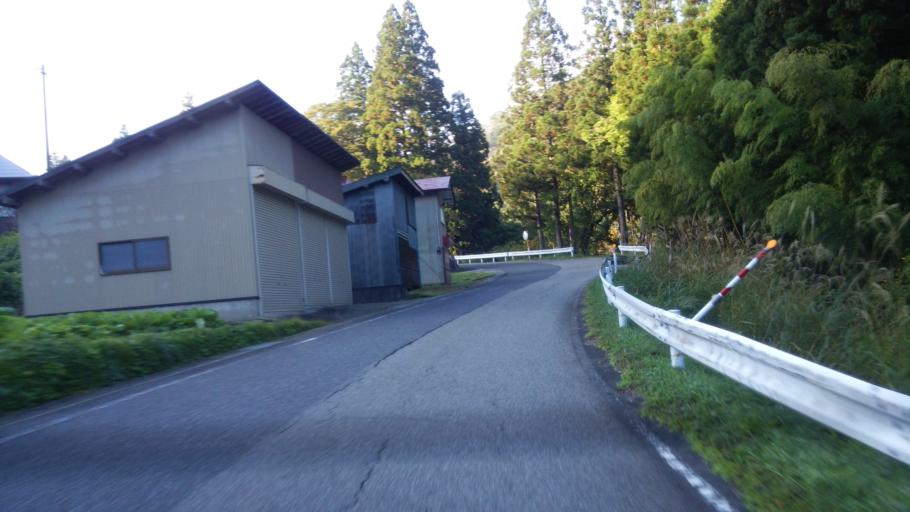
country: JP
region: Fukushima
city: Kitakata
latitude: 37.4238
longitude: 139.7252
